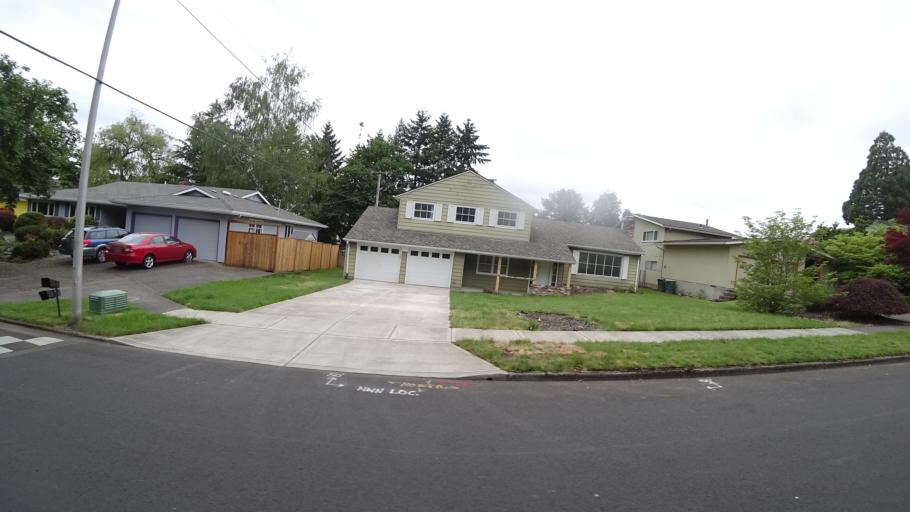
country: US
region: Oregon
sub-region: Washington County
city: Raleigh Hills
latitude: 45.4748
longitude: -122.7748
